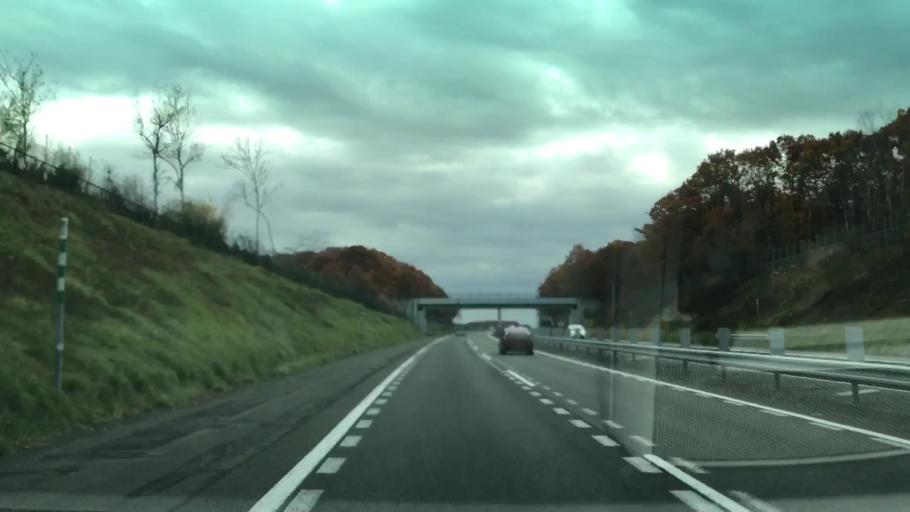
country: JP
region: Hokkaido
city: Kitahiroshima
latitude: 42.9198
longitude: 141.5449
